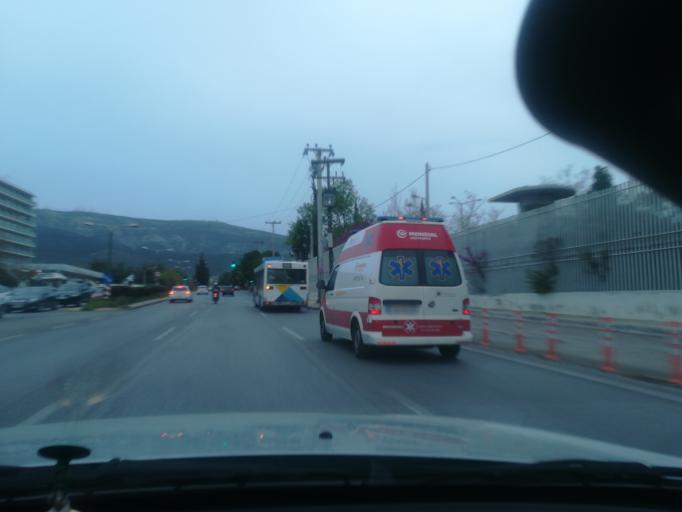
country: GR
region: Attica
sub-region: Nomarchia Athinas
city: Papagou
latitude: 37.9899
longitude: 23.7777
